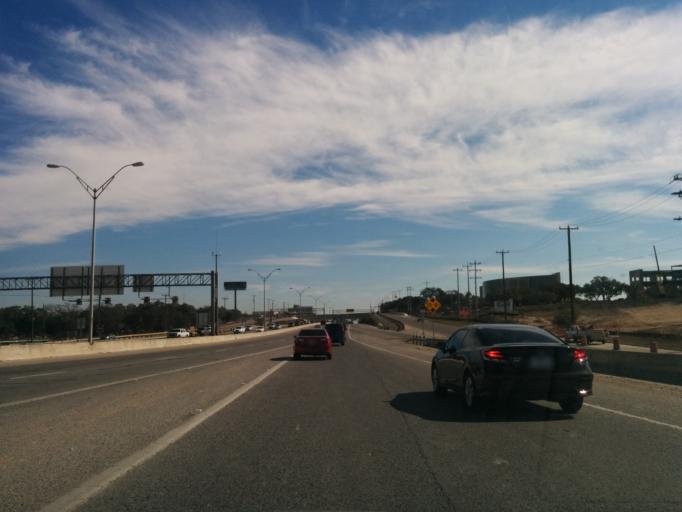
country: US
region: Texas
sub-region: Bexar County
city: Shavano Park
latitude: 29.5912
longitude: -98.5945
